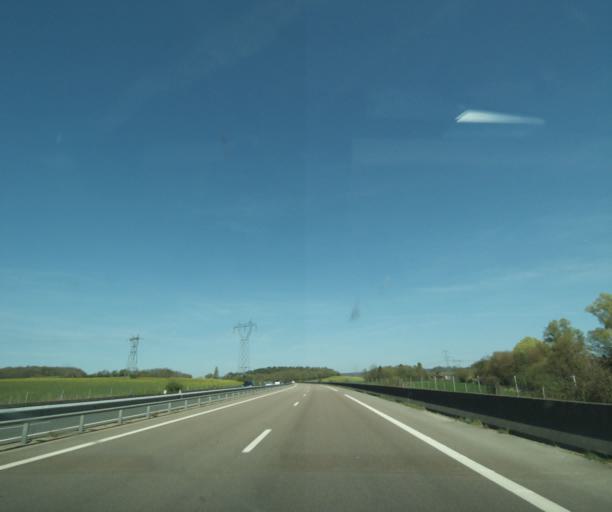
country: FR
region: Bourgogne
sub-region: Departement de la Nievre
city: Pougues-les-Eaux
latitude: 47.0562
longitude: 3.1318
